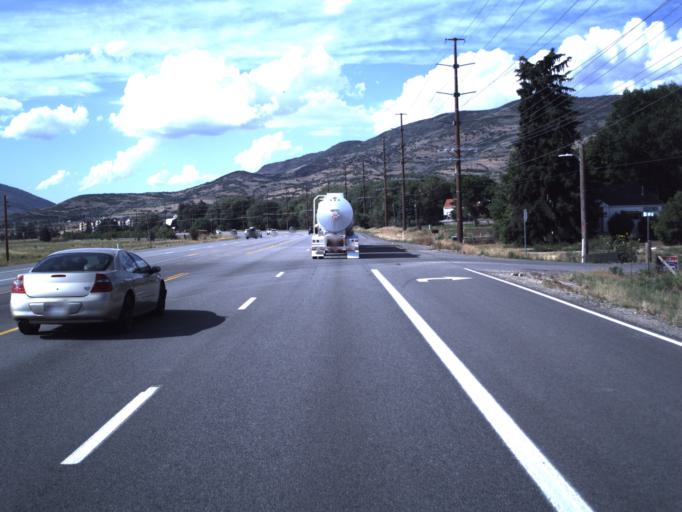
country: US
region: Utah
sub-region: Wasatch County
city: Heber
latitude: 40.5305
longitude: -111.4093
